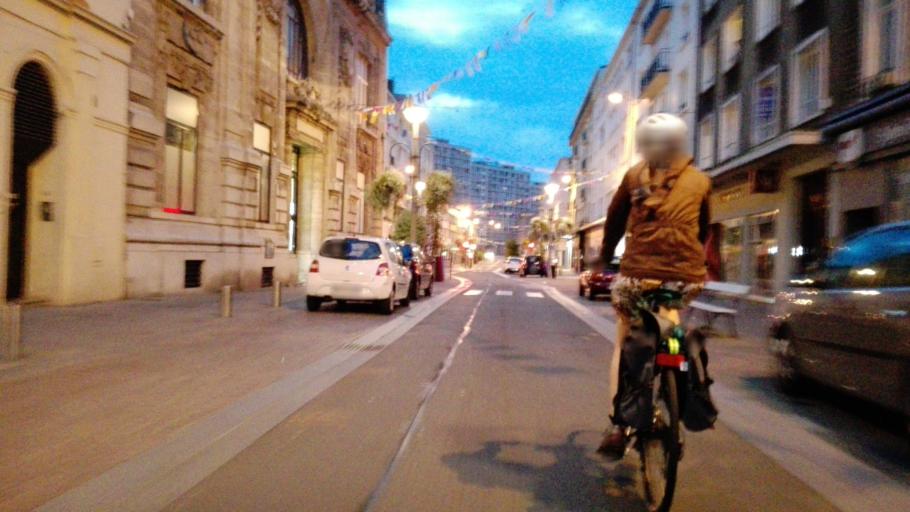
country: FR
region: Nord-Pas-de-Calais
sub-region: Departement du Pas-de-Calais
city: Boulogne-sur-Mer
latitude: 50.7236
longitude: 1.6046
